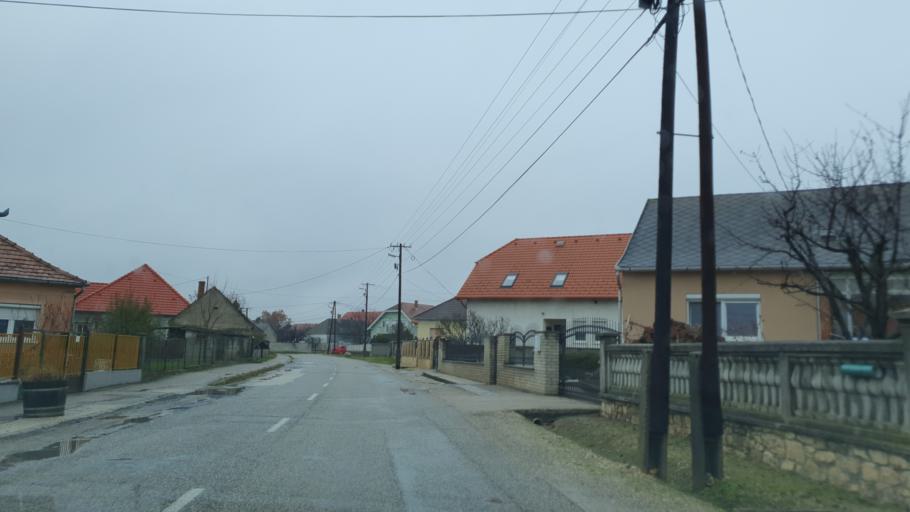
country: HU
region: Veszprem
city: Hajmasker
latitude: 47.1440
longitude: 17.9544
